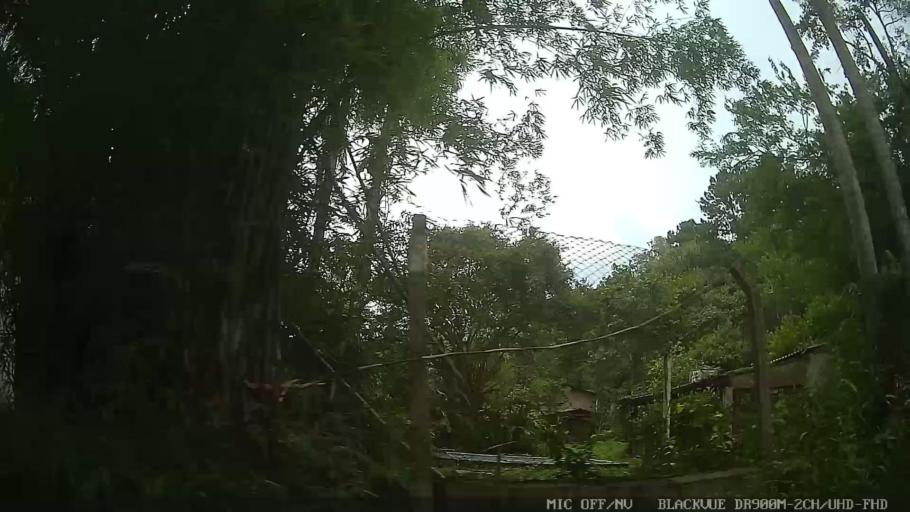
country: BR
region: Sao Paulo
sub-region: Aruja
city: Aruja
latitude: -23.4495
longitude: -46.2896
